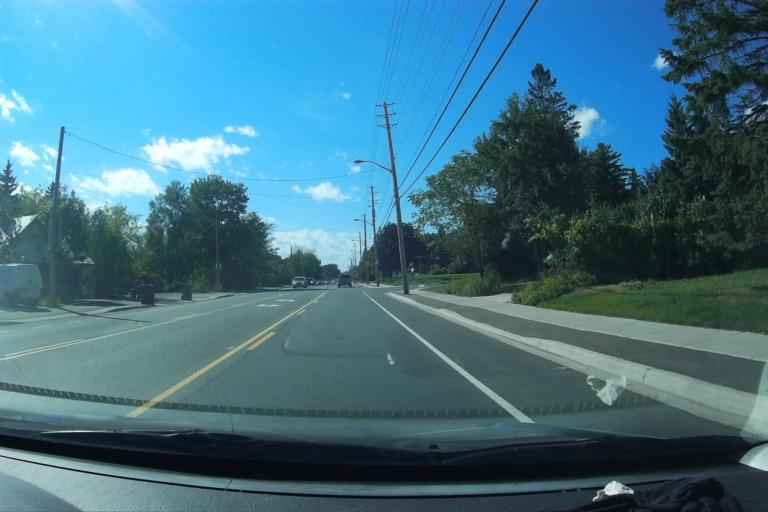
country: CA
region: Ontario
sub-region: Algoma
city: Sault Ste. Marie
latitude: 46.5049
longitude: -84.3098
